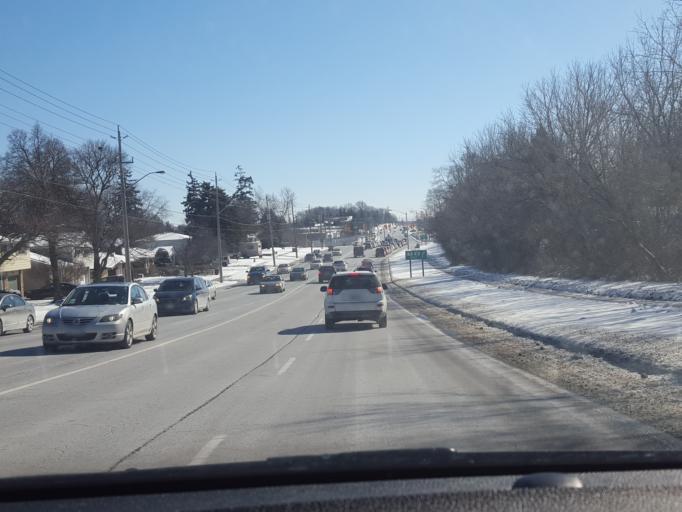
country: CA
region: Ontario
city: Kitchener
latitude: 43.4228
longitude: -80.5184
